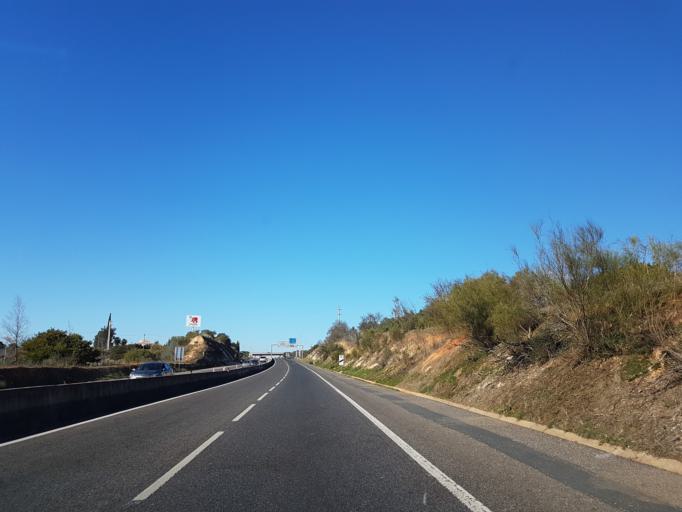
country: PT
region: Faro
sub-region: Lagoa
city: Lagoa
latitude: 37.1371
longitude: -8.4631
